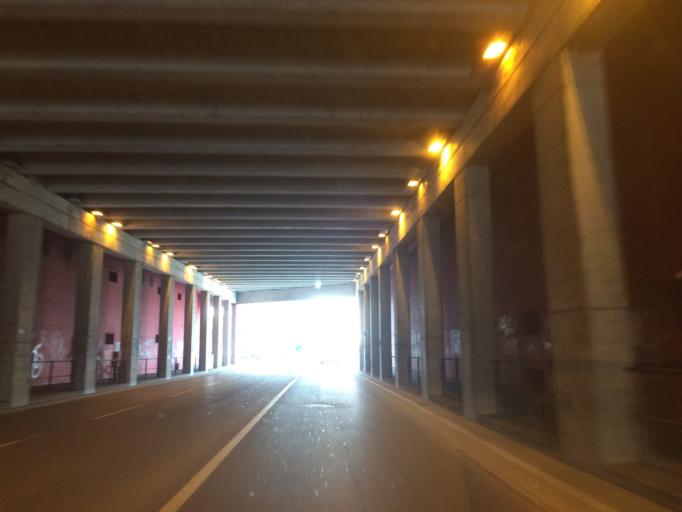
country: IT
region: Lombardy
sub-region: Provincia di Brescia
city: Brescia
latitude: 45.5366
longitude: 10.2086
